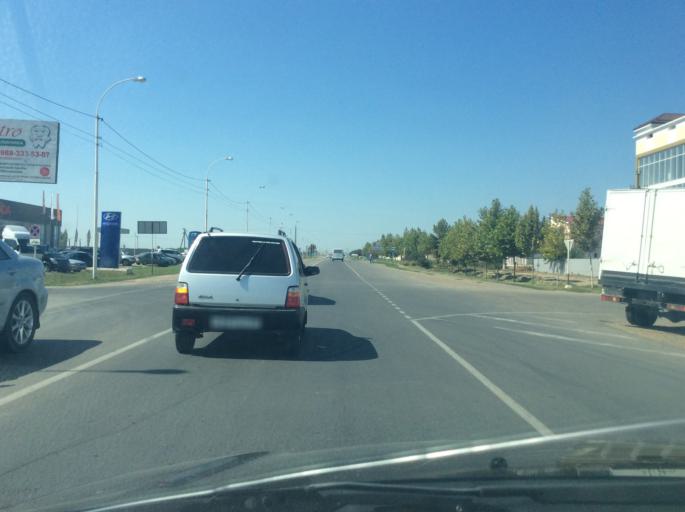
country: RU
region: Krasnodarskiy
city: Slavyansk-na-Kubani
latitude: 45.2491
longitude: 38.0926
